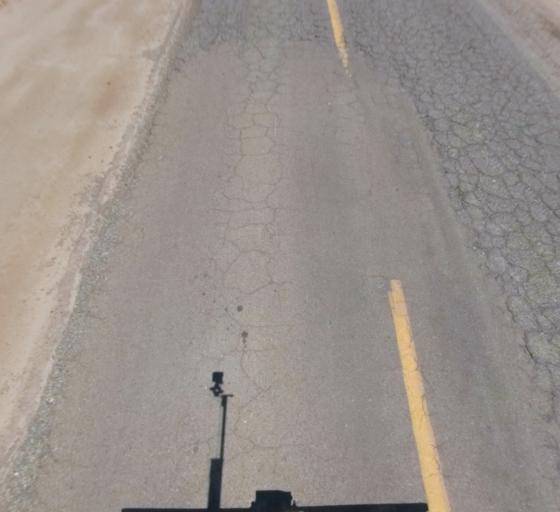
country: US
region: California
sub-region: Madera County
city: Parkwood
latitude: 36.8658
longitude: -120.0893
